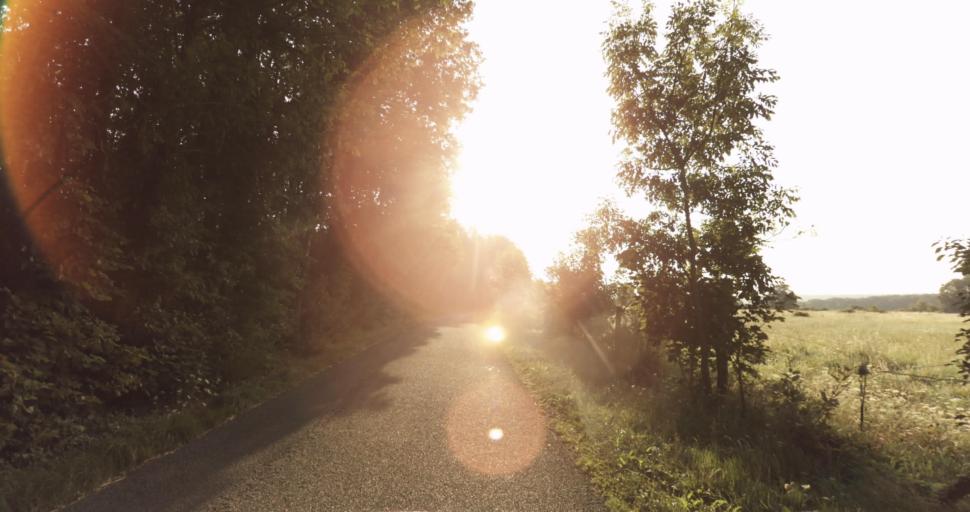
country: FR
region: Centre
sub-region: Departement d'Eure-et-Loir
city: Vert-en-Drouais
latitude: 48.7747
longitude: 1.3143
